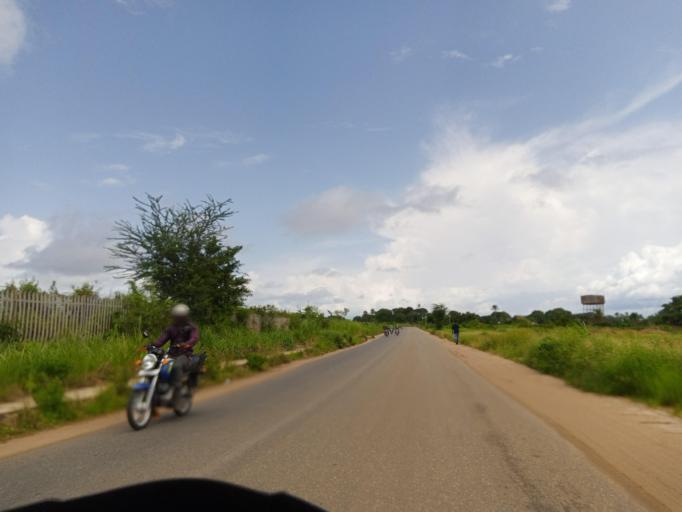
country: SL
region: Northern Province
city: Tintafor
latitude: 8.6220
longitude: -13.2132
